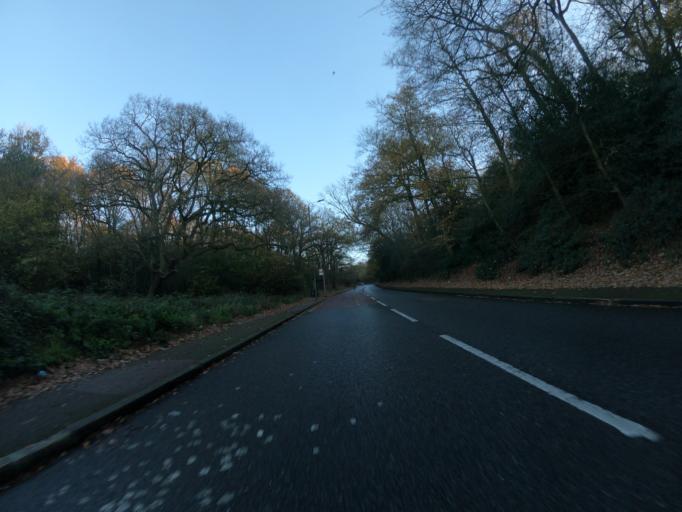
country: GB
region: England
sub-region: Greater London
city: Abbey Wood
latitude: 51.4835
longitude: 0.1103
